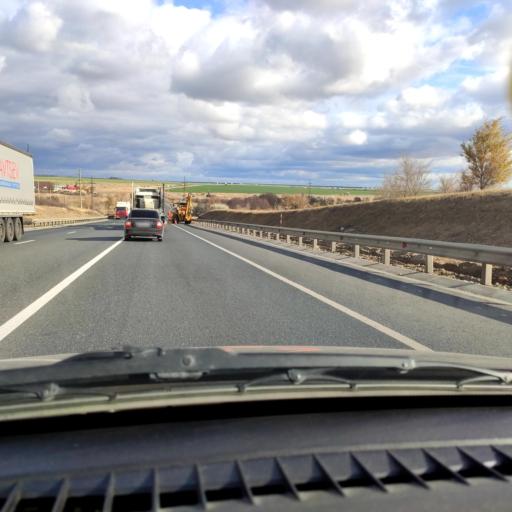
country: RU
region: Samara
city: Varlamovo
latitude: 53.2005
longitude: 48.3771
